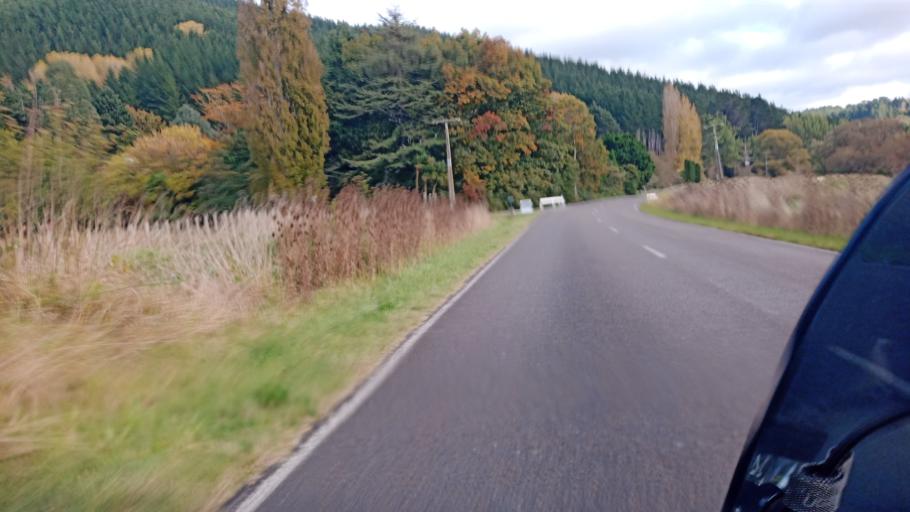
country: NZ
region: Gisborne
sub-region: Gisborne District
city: Gisborne
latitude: -38.5697
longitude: 177.7254
